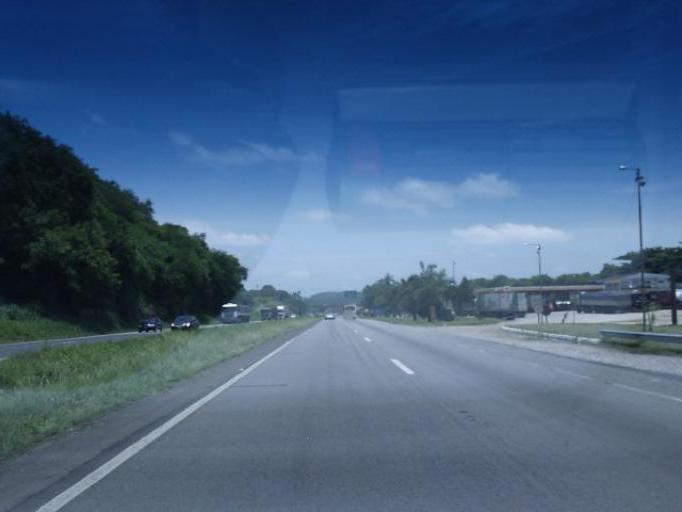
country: BR
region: Sao Paulo
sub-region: Miracatu
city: Miracatu
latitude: -24.2868
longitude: -47.4498
